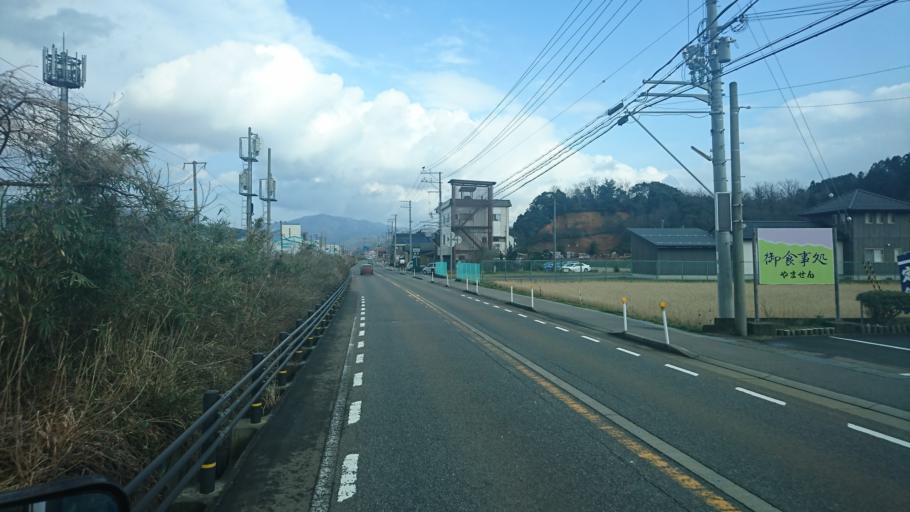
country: JP
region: Tottori
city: Tottori
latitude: 35.6191
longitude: 134.4580
